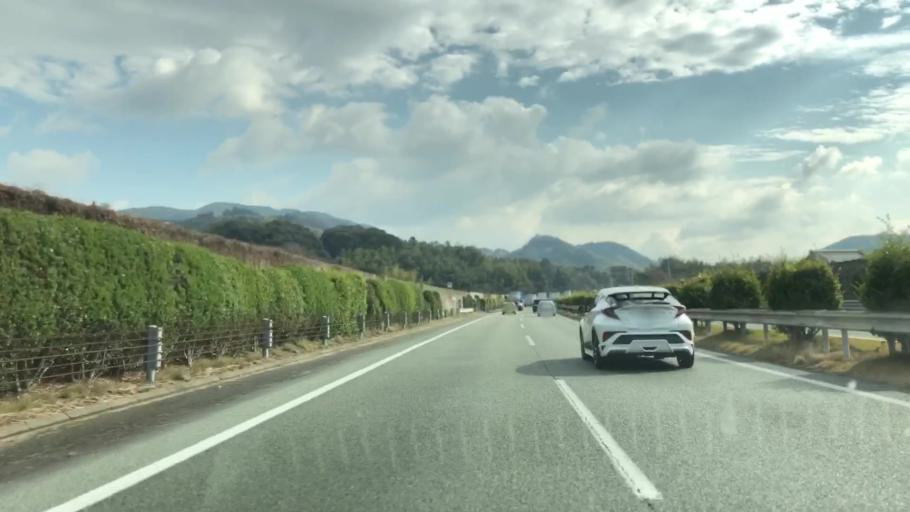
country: JP
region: Fukuoka
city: Setakamachi-takayanagi
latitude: 33.1143
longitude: 130.5295
